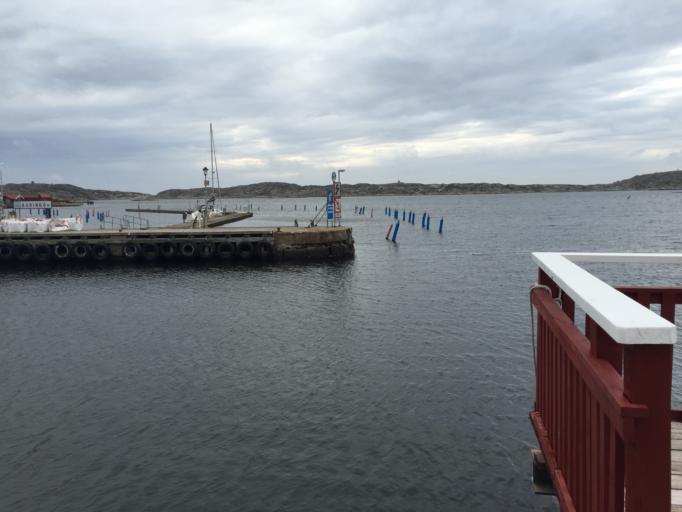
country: SE
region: Vaestra Goetaland
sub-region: Lysekils Kommun
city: Lysekil
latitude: 58.1132
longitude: 11.3668
